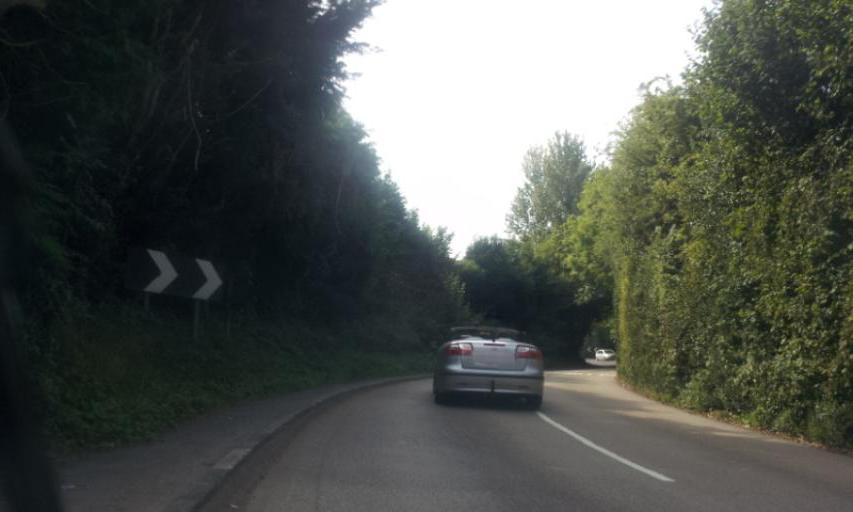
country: GB
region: England
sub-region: Kent
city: Paddock Wood
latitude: 51.1604
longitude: 0.3811
